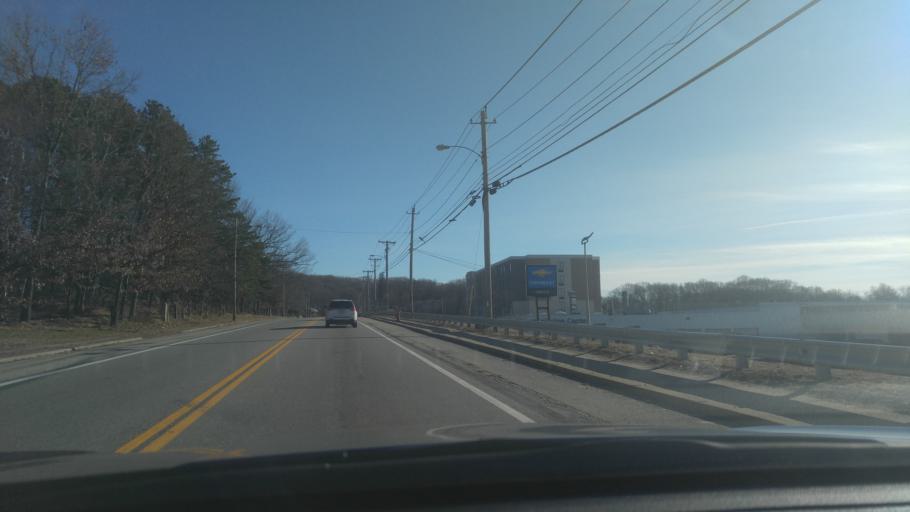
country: US
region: Rhode Island
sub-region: Providence County
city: Cumberland Hill
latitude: 41.9935
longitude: -71.4857
